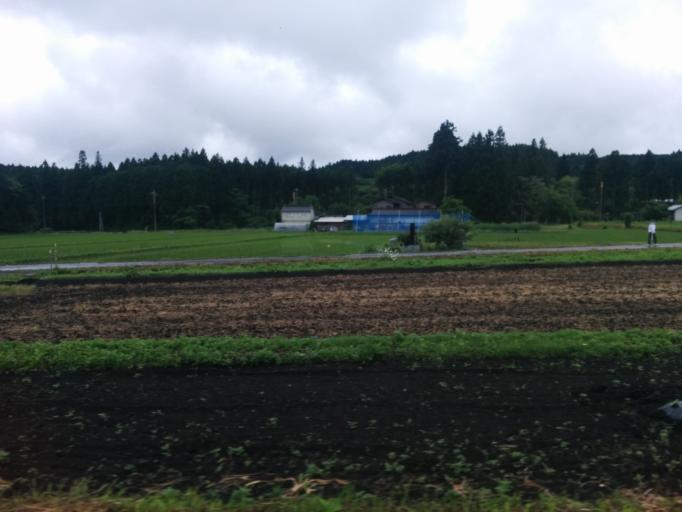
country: JP
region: Tochigi
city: Imaichi
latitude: 36.7289
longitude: 139.6639
